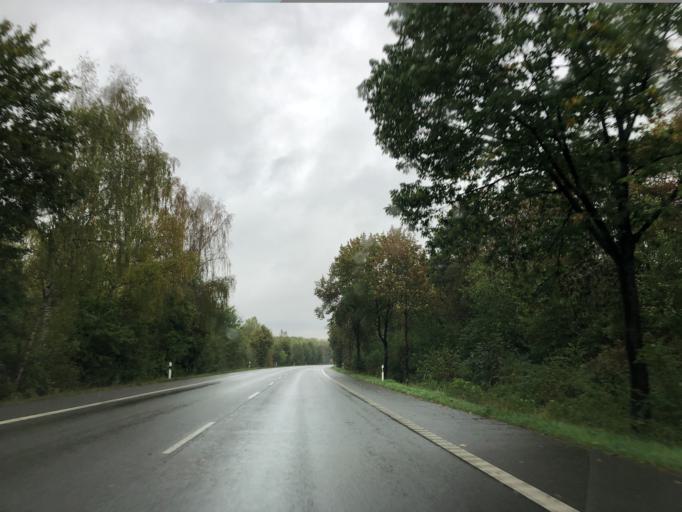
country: DE
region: North Rhine-Westphalia
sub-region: Regierungsbezirk Koln
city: Bedburg
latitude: 51.0289
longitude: 6.5767
